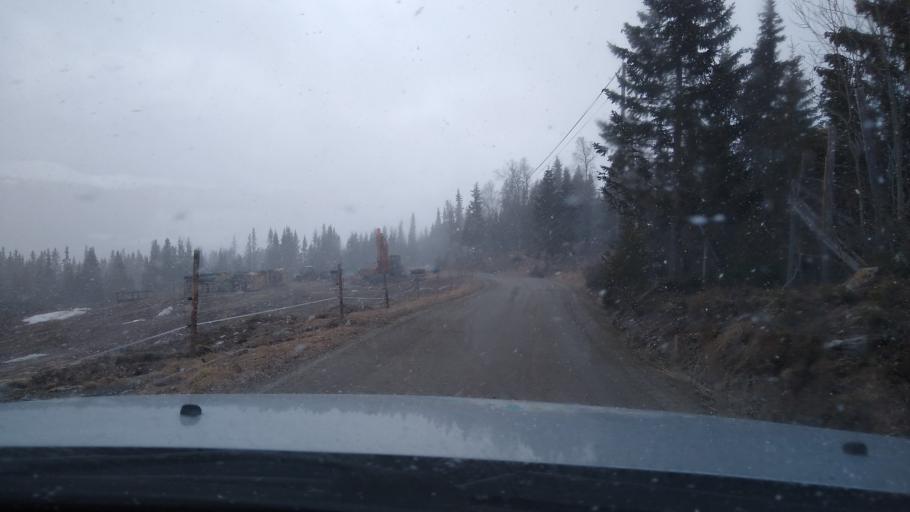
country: NO
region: Oppland
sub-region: Oyer
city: Tretten
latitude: 61.4637
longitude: 10.3453
